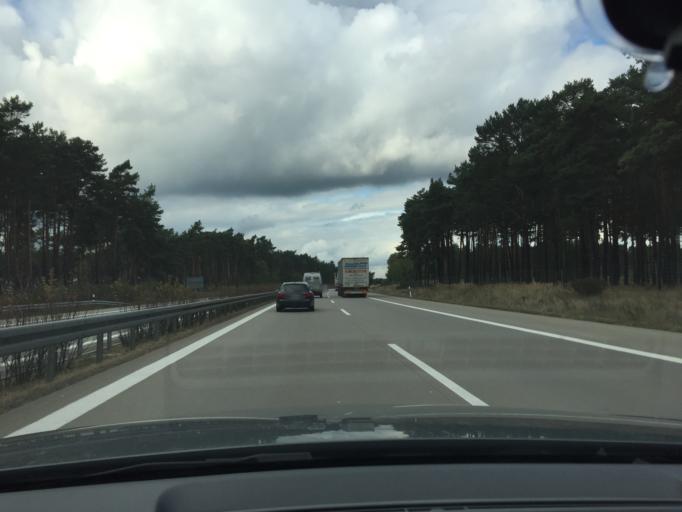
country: DE
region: Brandenburg
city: Kasel-Golzig
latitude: 51.9292
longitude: 13.7688
